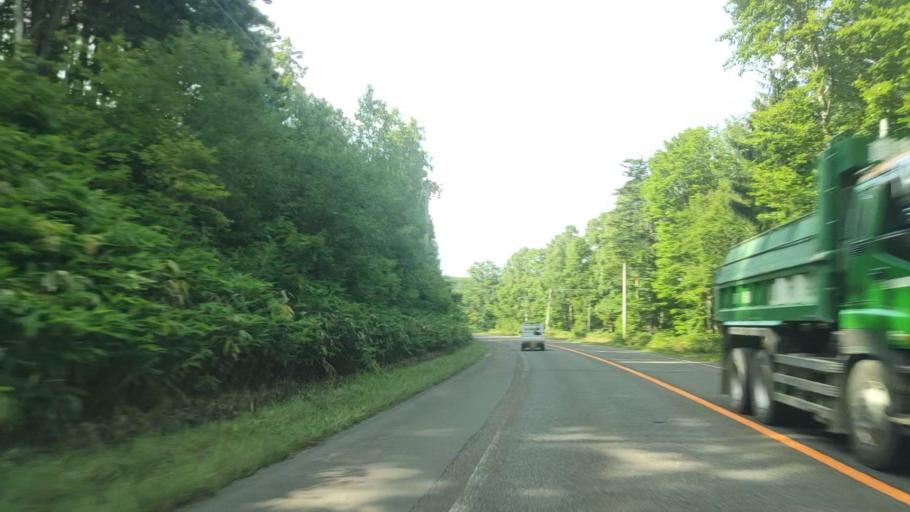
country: JP
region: Hokkaido
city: Nayoro
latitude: 44.3899
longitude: 142.3976
